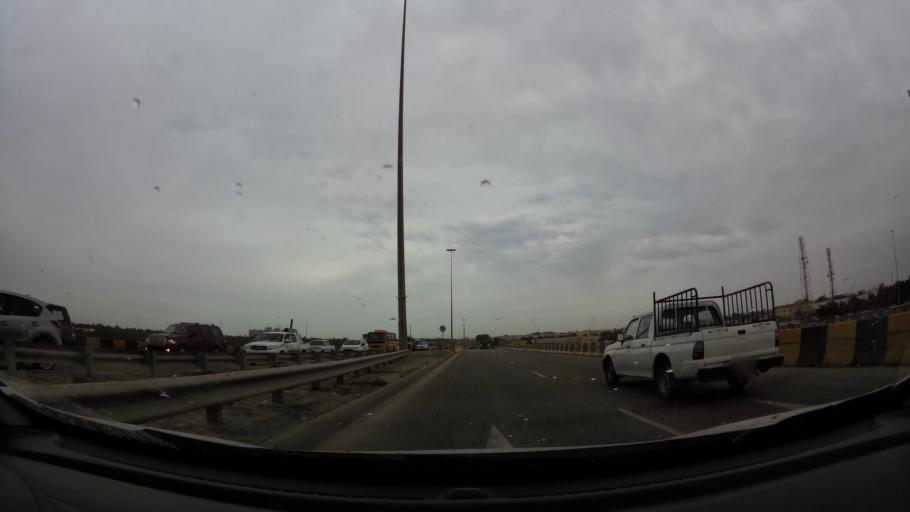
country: BH
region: Central Governorate
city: Madinat Hamad
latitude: 26.1729
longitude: 50.4654
